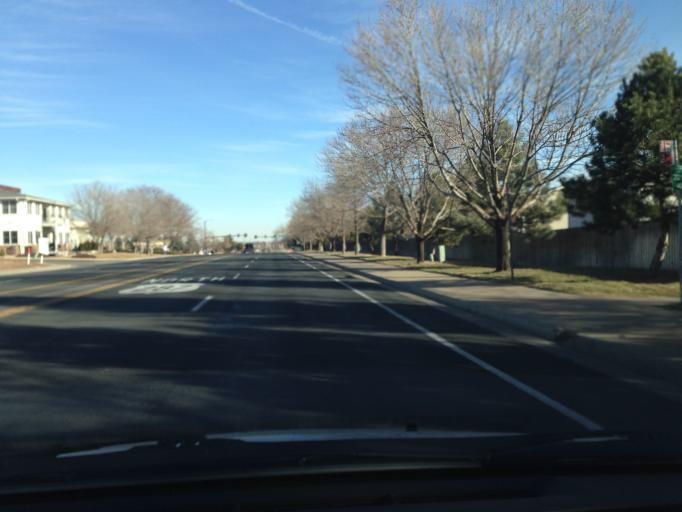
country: US
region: Colorado
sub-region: Boulder County
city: Lafayette
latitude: 40.0001
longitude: -105.1080
